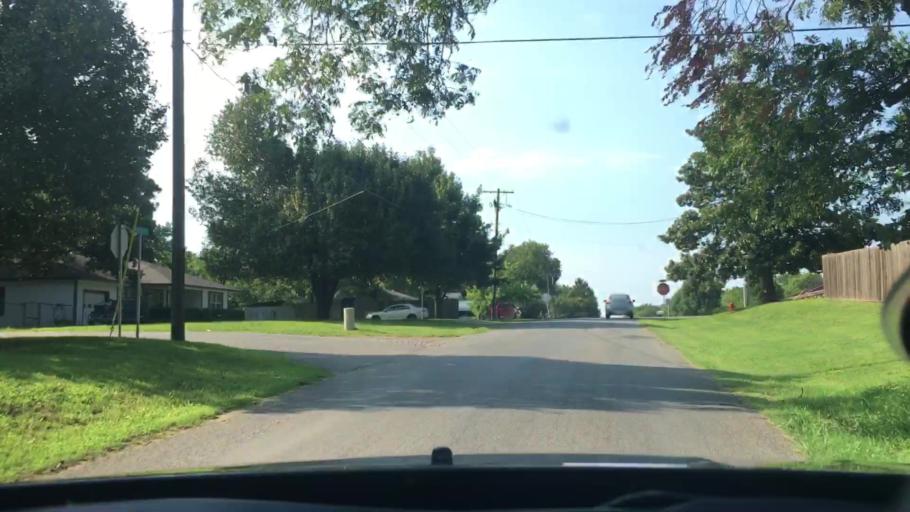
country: US
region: Oklahoma
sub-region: Johnston County
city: Tishomingo
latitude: 34.2239
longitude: -96.6711
